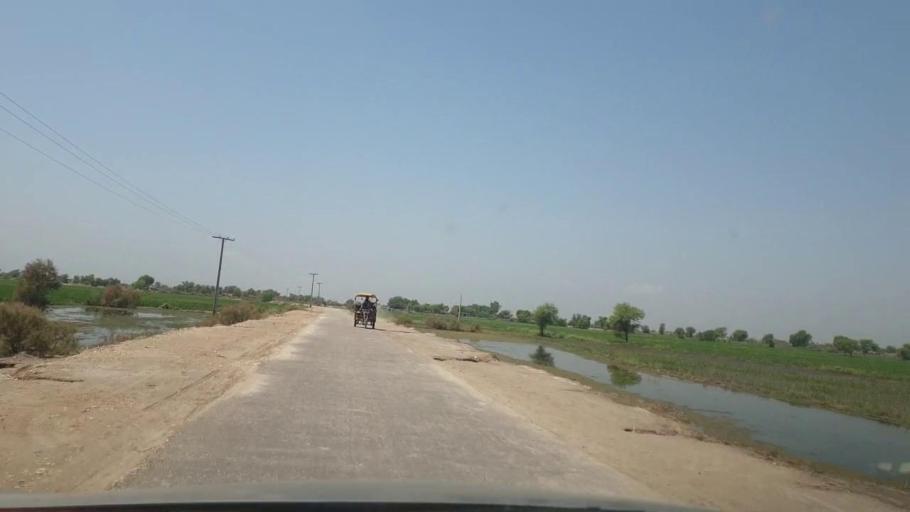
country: PK
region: Sindh
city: Warah
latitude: 27.4837
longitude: 67.7418
